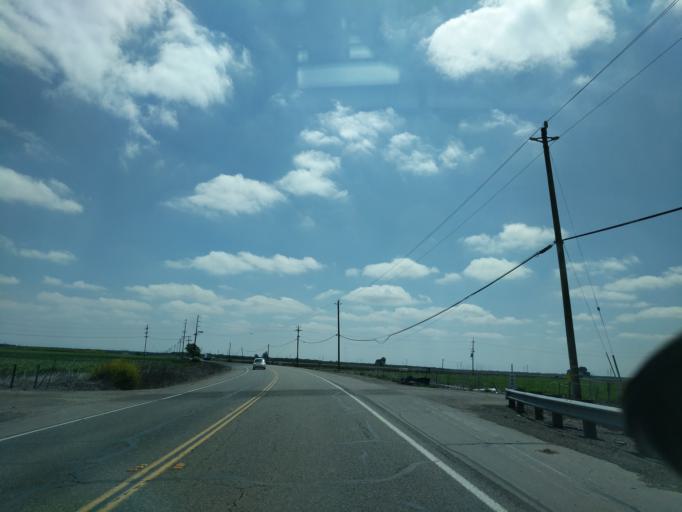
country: US
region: California
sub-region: San Joaquin County
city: Garden Acres
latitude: 37.9493
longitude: -121.1821
